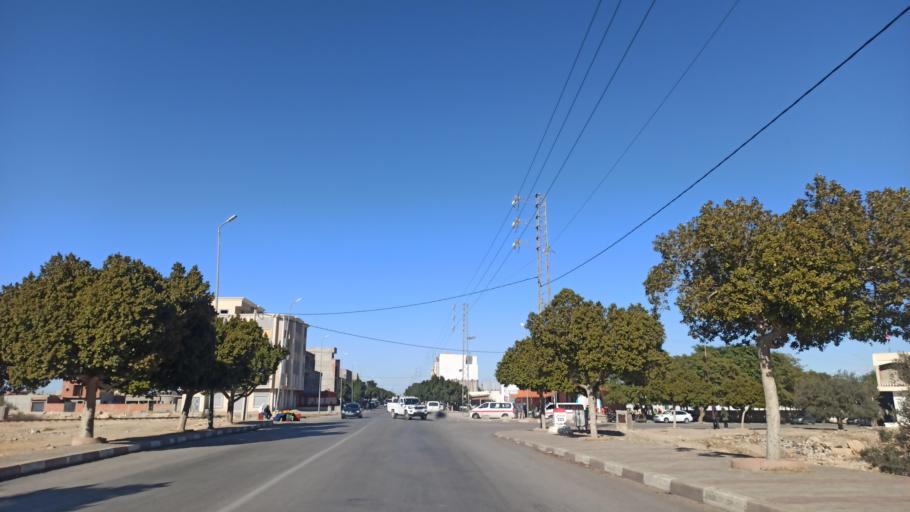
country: TN
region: Sidi Bu Zayd
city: Jilma
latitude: 35.2714
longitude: 9.4191
